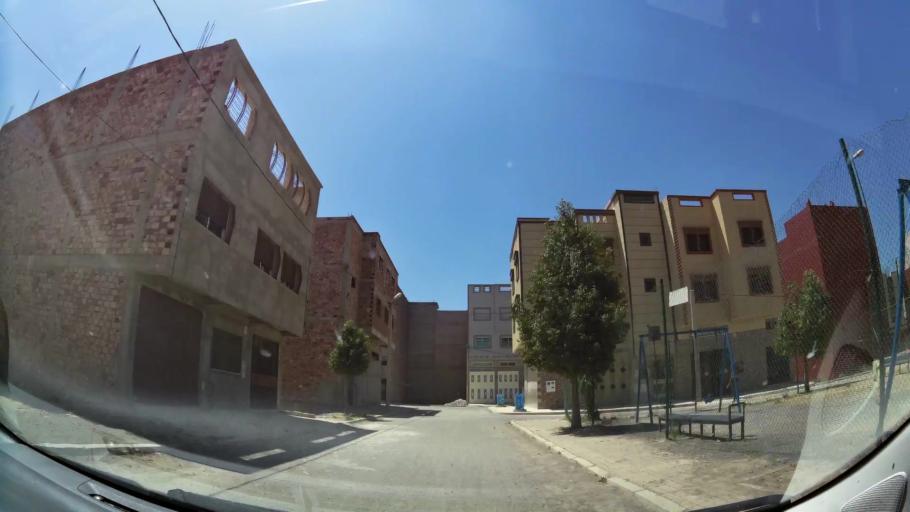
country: MA
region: Oriental
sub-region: Oujda-Angad
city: Oujda
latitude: 34.6862
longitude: -1.9465
